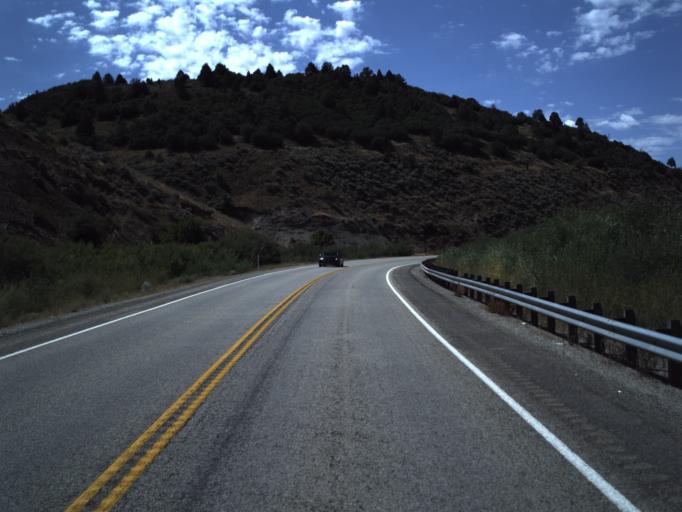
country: US
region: Utah
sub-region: Utah County
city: Woodland Hills
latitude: 39.9887
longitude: -111.4990
